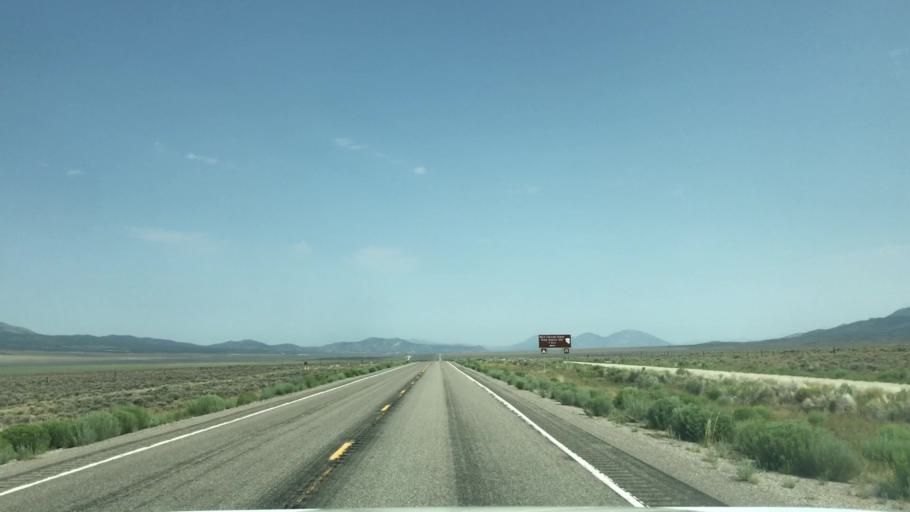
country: US
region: Nevada
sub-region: White Pine County
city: Ely
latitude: 39.0864
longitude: -114.7503
